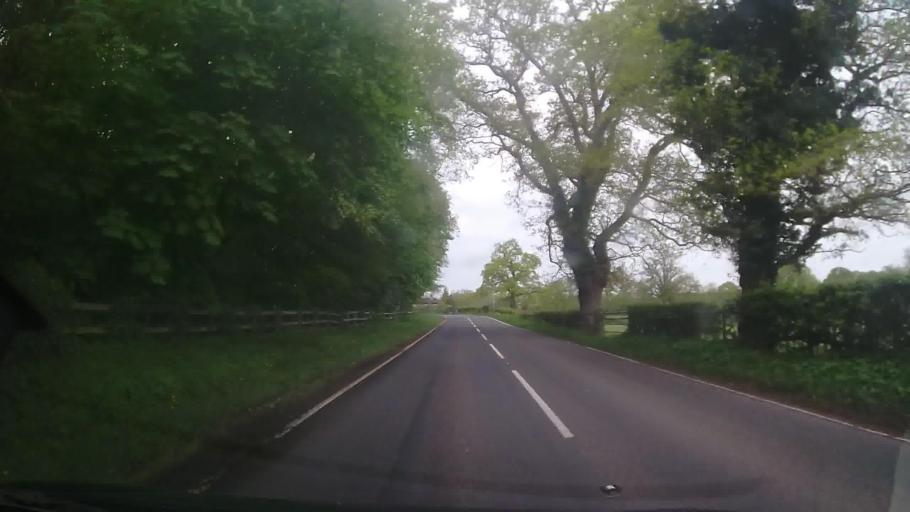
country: GB
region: Wales
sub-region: Wrexham
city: Overton
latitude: 52.9824
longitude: -2.9673
